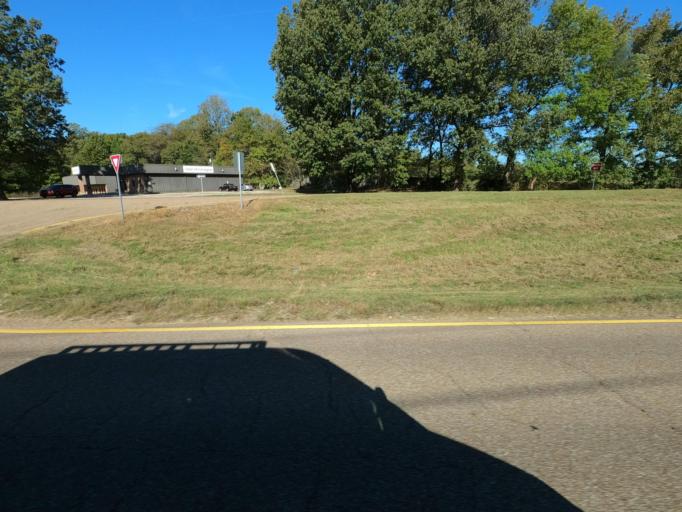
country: US
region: Tennessee
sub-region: Tipton County
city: Brighton
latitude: 35.5184
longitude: -89.6994
